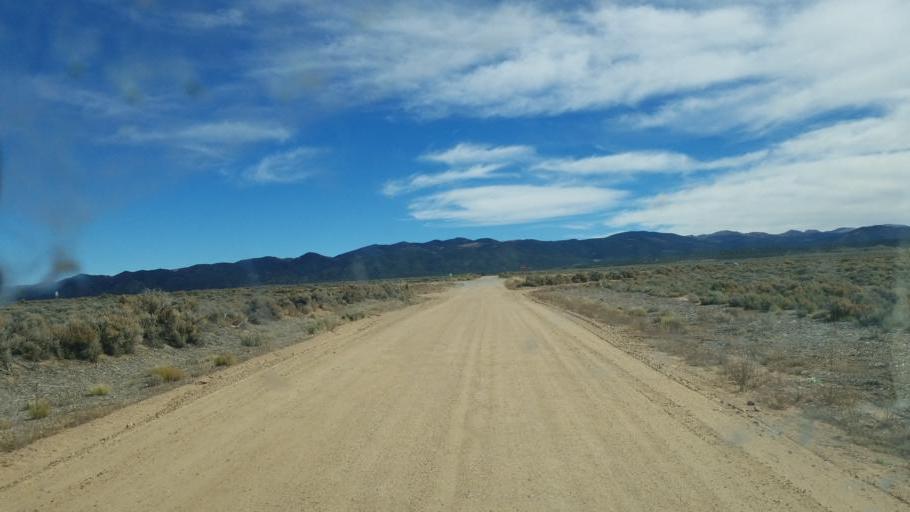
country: US
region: Colorado
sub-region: Costilla County
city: San Luis
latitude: 37.2868
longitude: -105.4351
